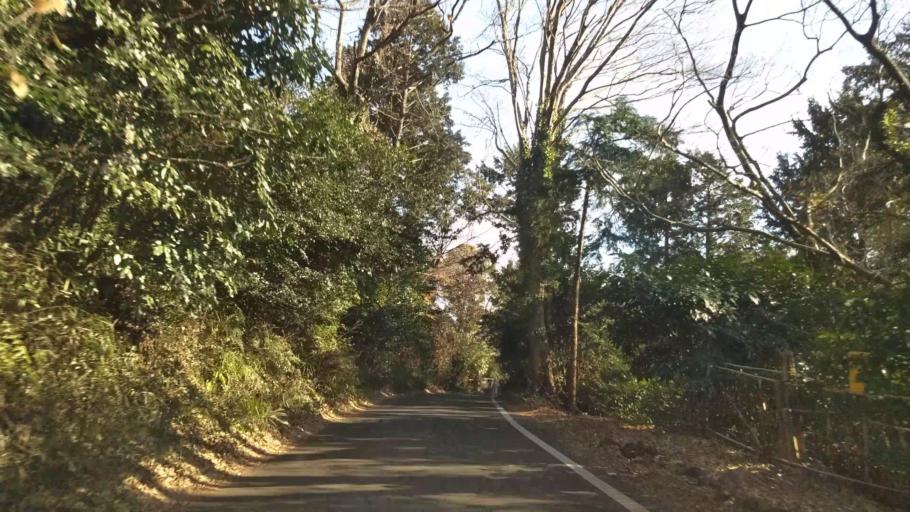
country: JP
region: Kanagawa
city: Hadano
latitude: 35.3698
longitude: 139.2473
